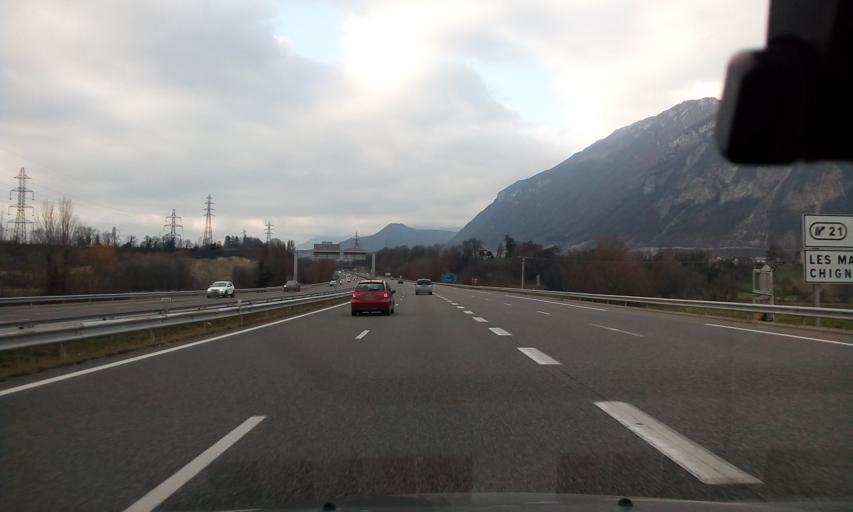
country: FR
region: Rhone-Alpes
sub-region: Departement de la Savoie
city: Les Marches
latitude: 45.4923
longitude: 6.0230
